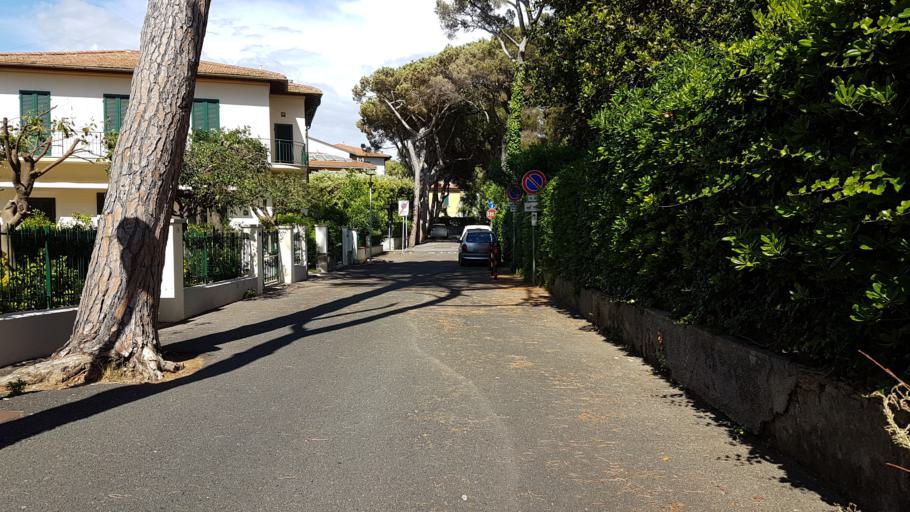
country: IT
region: Tuscany
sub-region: Provincia di Livorno
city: Rosignano Solvay-Castiglioncello
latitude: 43.4028
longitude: 10.4210
